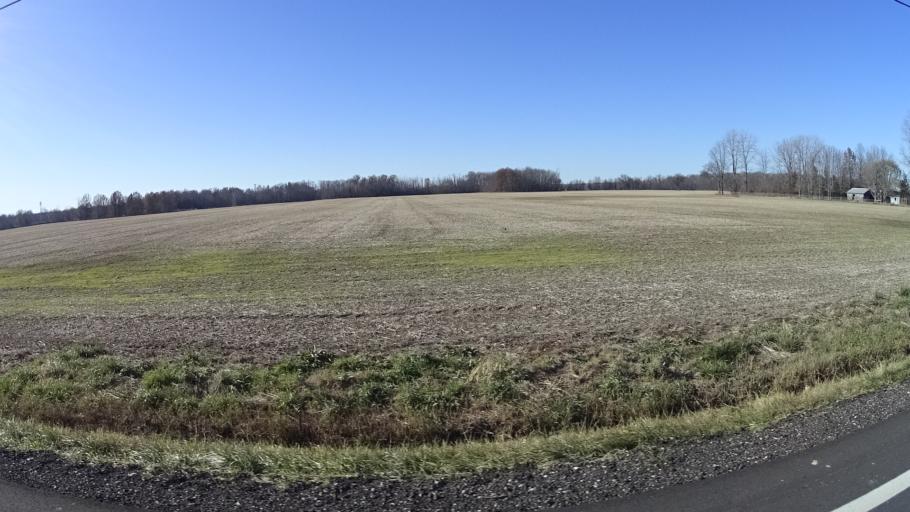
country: US
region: Ohio
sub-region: Lorain County
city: Lagrange
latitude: 41.2892
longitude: -82.1181
